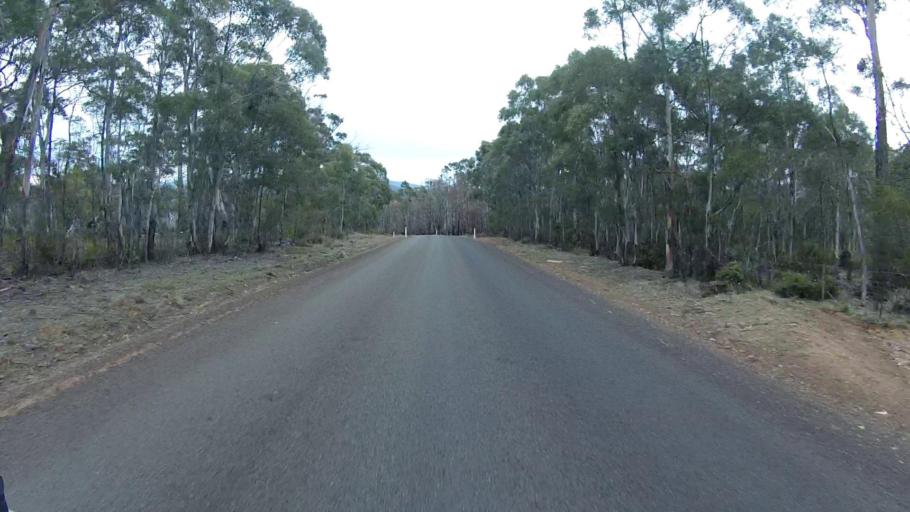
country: AU
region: Tasmania
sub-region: Sorell
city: Sorell
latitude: -42.5800
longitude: 147.8803
